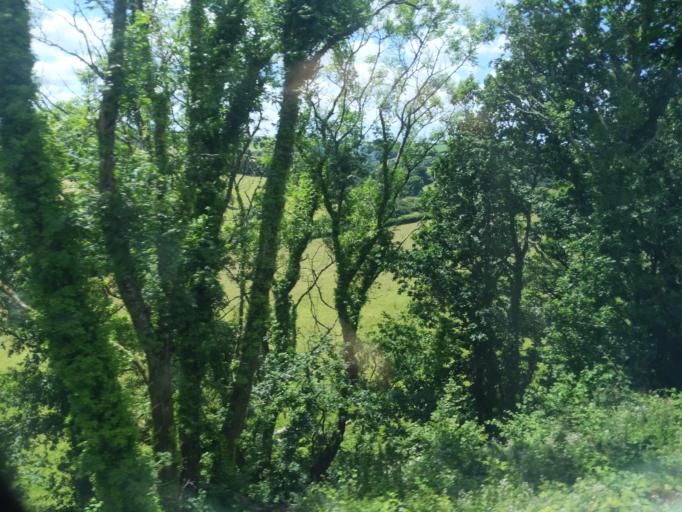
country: GB
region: England
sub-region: Cornwall
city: Liskeard
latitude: 50.4435
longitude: -4.4596
